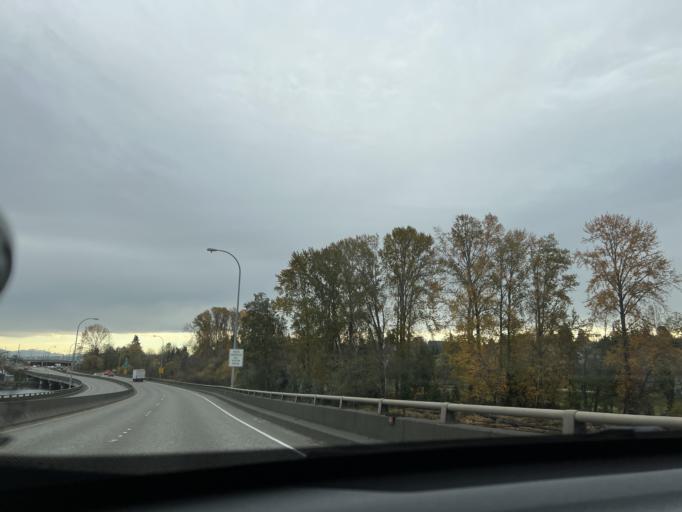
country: US
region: Washington
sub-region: King County
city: Seattle
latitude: 47.6433
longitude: -122.3113
